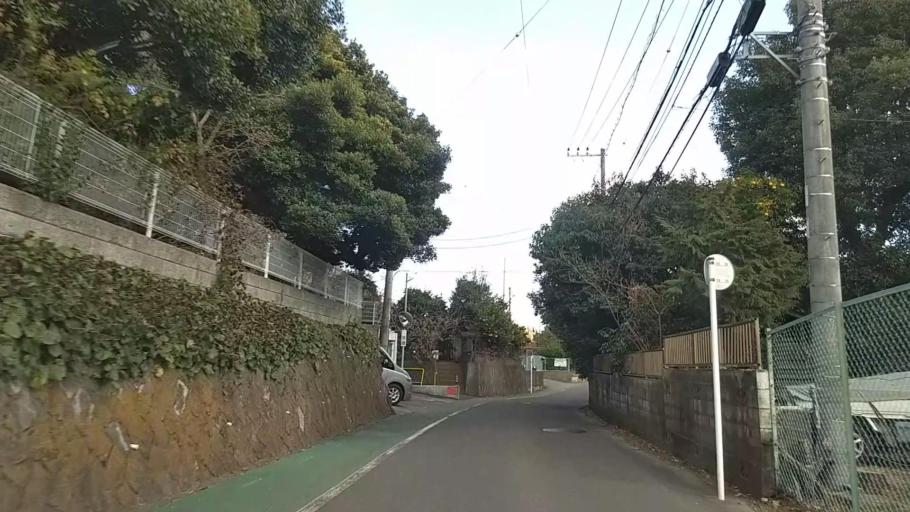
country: JP
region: Kanagawa
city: Isehara
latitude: 35.4061
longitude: 139.3151
